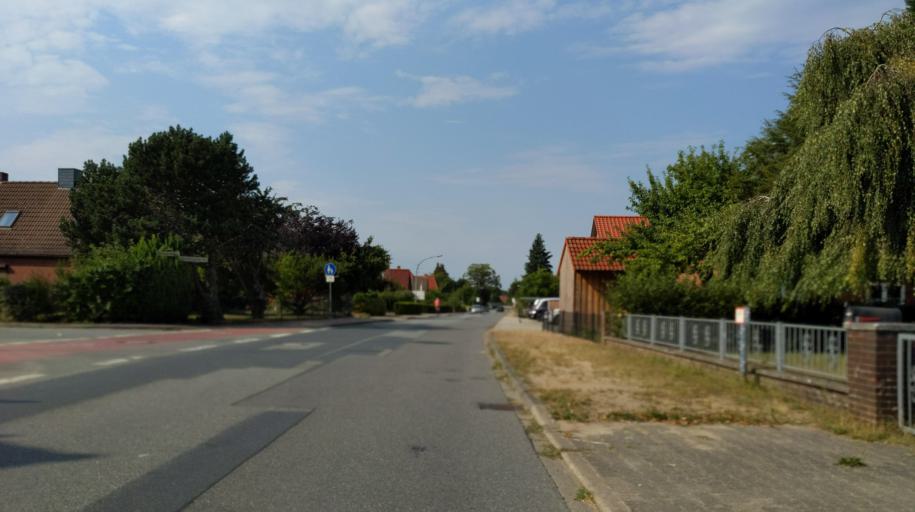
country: DE
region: Schleswig-Holstein
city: Berkenthin
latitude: 53.7361
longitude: 10.6377
